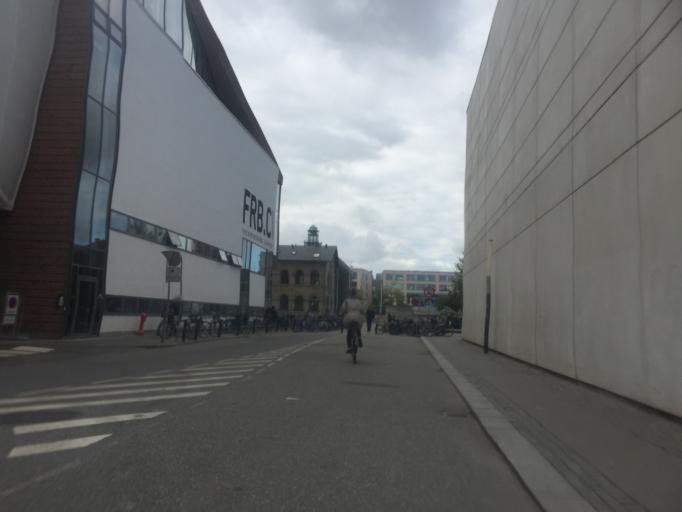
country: DK
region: Capital Region
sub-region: Frederiksberg Kommune
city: Frederiksberg
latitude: 55.6819
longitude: 12.5309
